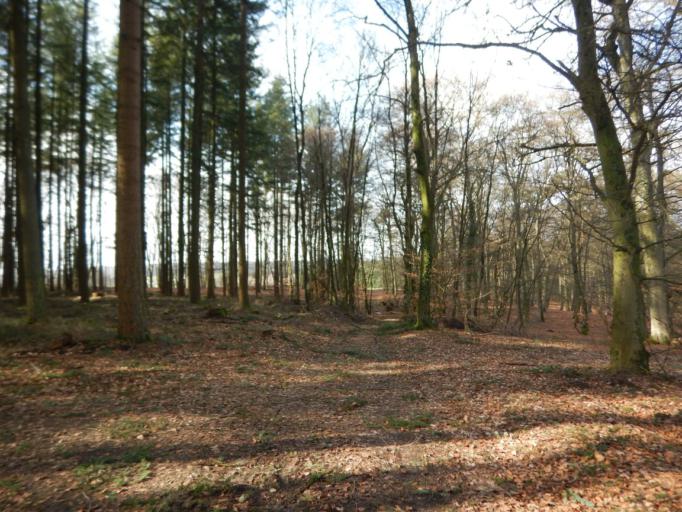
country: LU
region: Grevenmacher
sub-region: Canton d'Echternach
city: Bech
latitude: 49.7658
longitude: 6.4028
